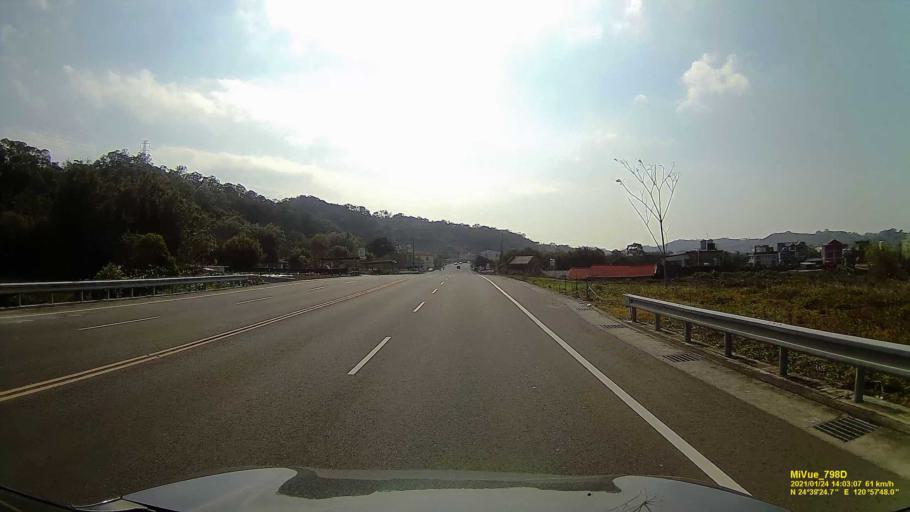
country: TW
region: Taiwan
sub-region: Hsinchu
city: Hsinchu
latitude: 24.6565
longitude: 120.9630
